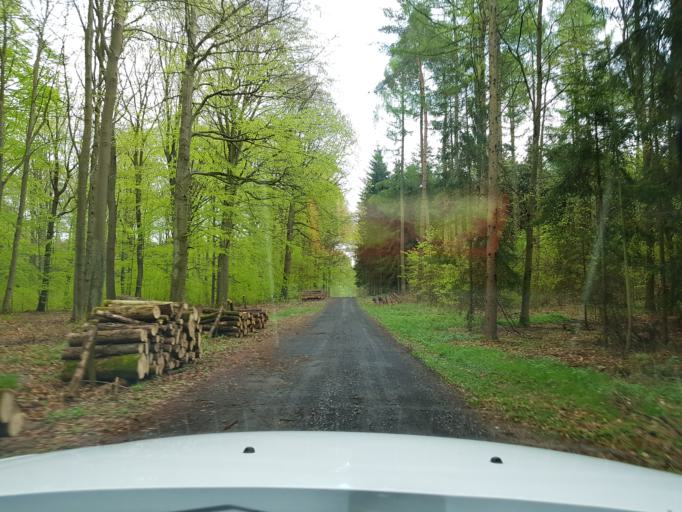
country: PL
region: West Pomeranian Voivodeship
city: Trzcinsko Zdroj
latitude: 52.9959
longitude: 14.6483
